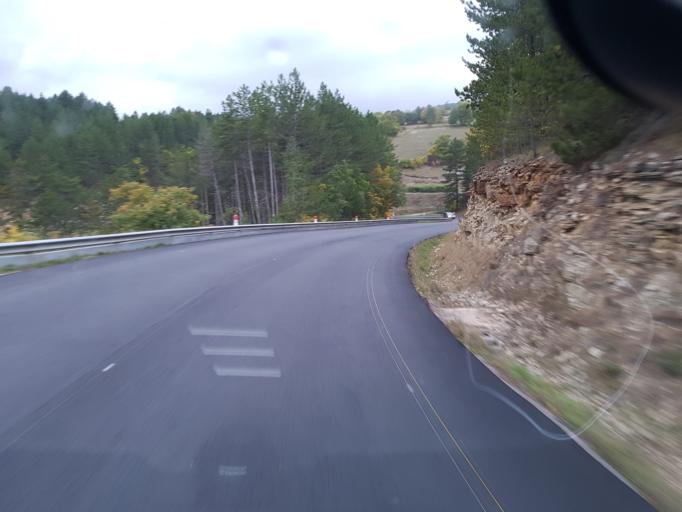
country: FR
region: Languedoc-Roussillon
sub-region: Departement de la Lozere
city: Mende
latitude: 44.5361
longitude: 3.5834
